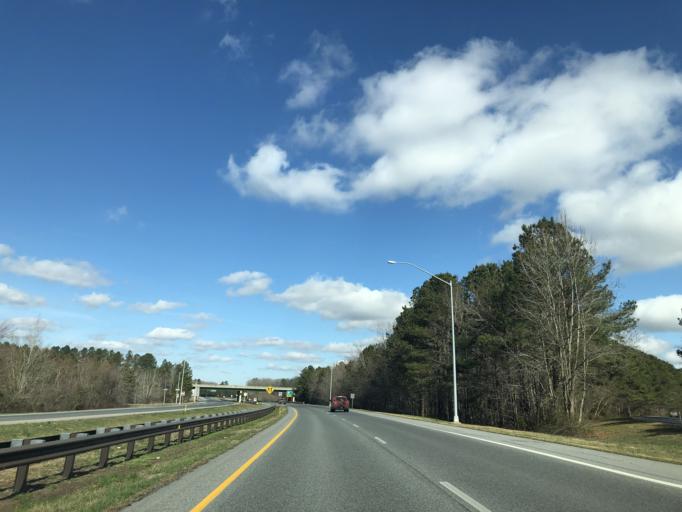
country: US
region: Maryland
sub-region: Worcester County
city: Berlin
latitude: 38.3741
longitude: -75.2065
